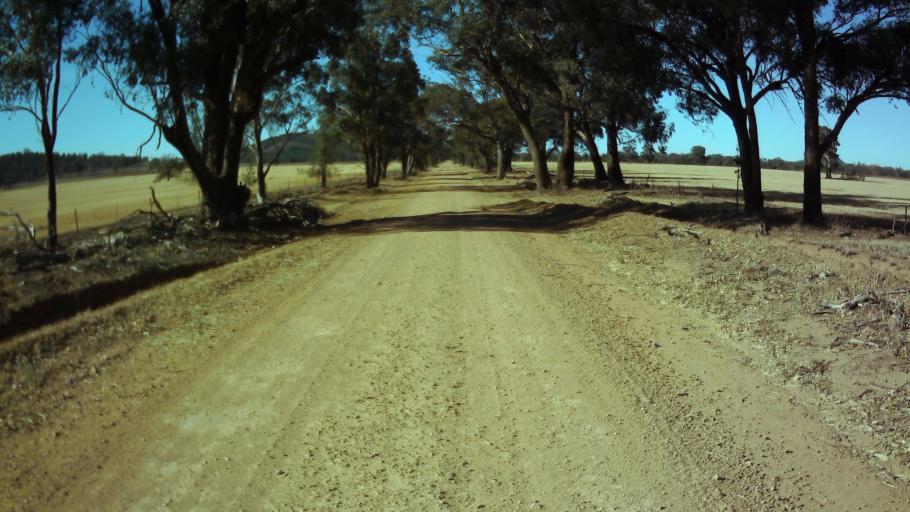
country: AU
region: New South Wales
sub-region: Weddin
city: Grenfell
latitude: -33.8060
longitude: 147.8782
